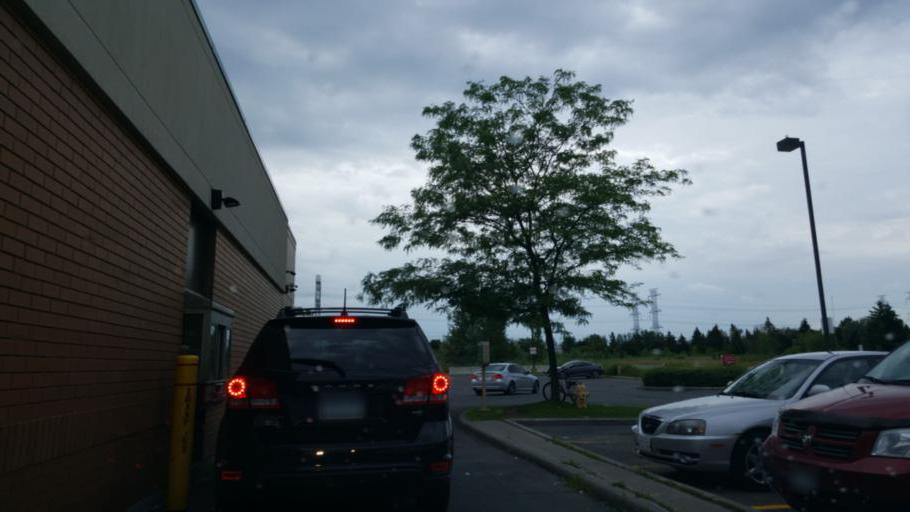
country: CA
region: Ontario
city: Ottawa
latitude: 45.3827
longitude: -75.6317
